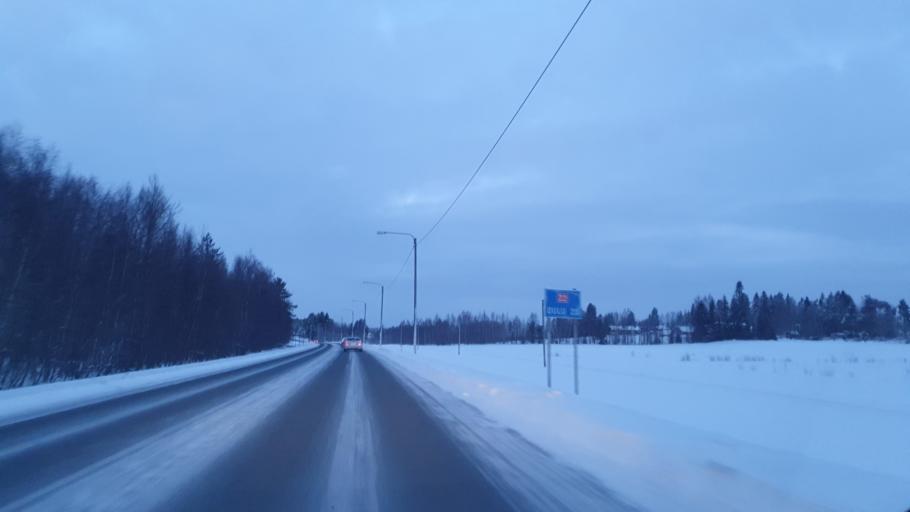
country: FI
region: Northern Ostrobothnia
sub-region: Oulu
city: Tyrnaevae
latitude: 64.9016
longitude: 25.7969
